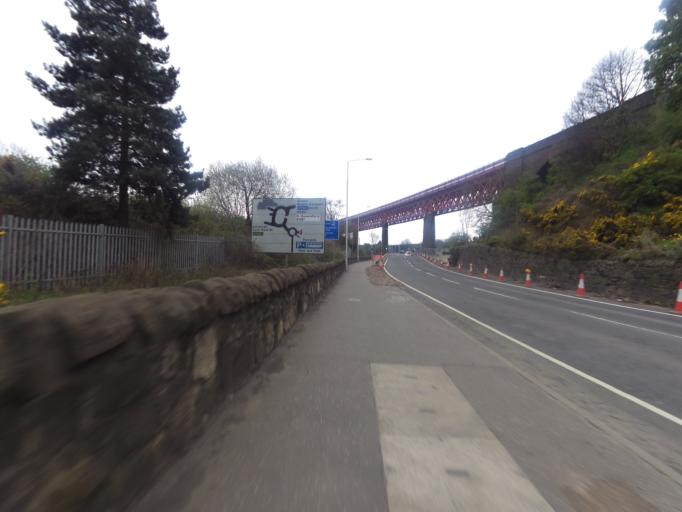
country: GB
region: Scotland
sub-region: Fife
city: Inverkeithing
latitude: 56.0234
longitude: -3.4044
